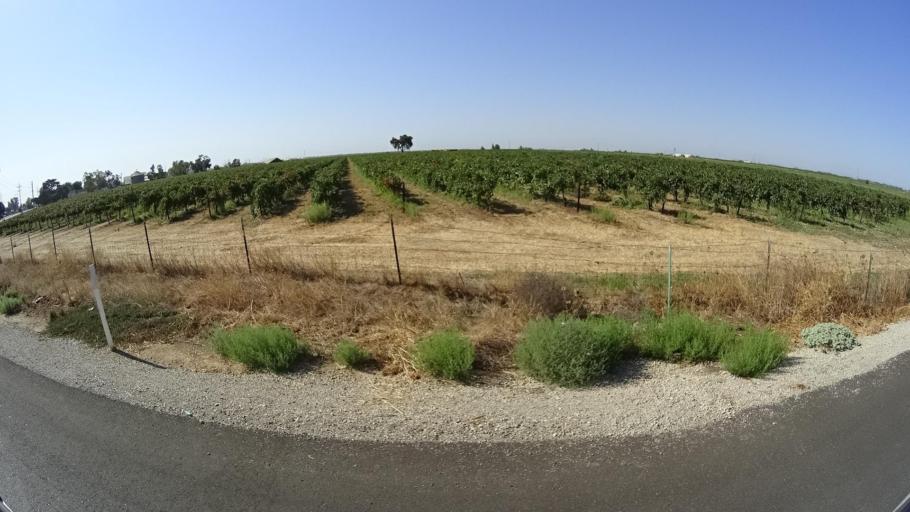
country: US
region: California
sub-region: Sacramento County
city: Elk Grove
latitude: 38.3723
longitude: -121.3599
